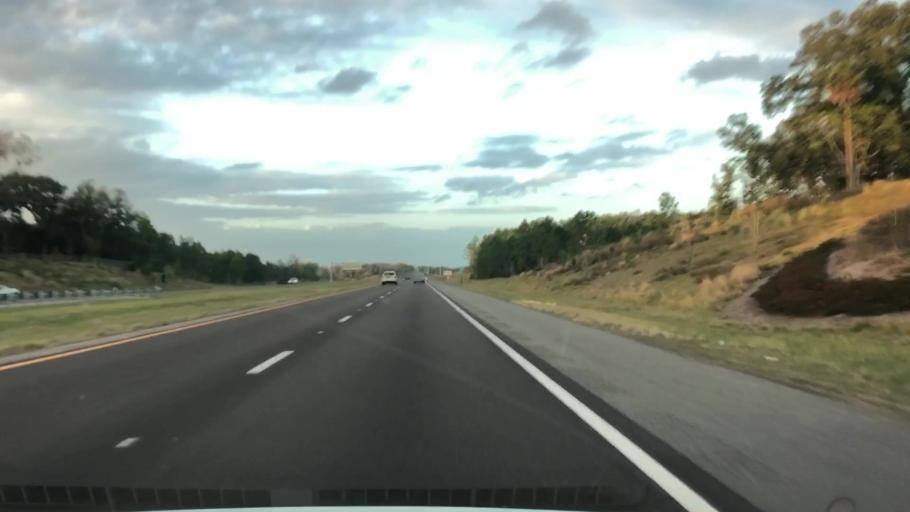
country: US
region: Florida
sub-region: Orange County
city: Zellwood
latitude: 28.7134
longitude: -81.5611
